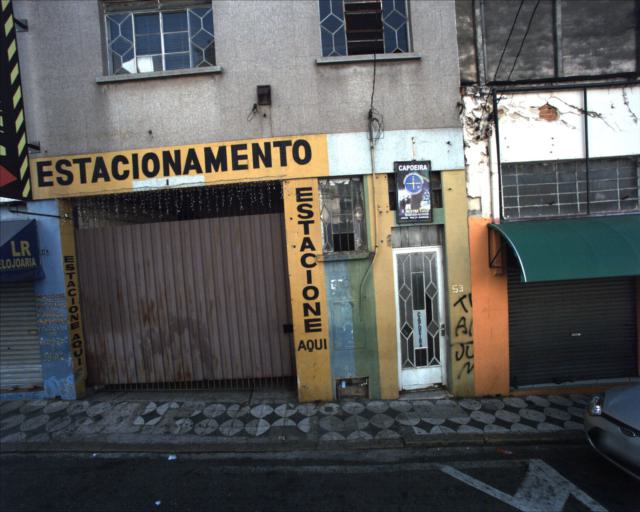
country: BR
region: Sao Paulo
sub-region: Sorocaba
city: Sorocaba
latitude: -23.5013
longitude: -47.4580
